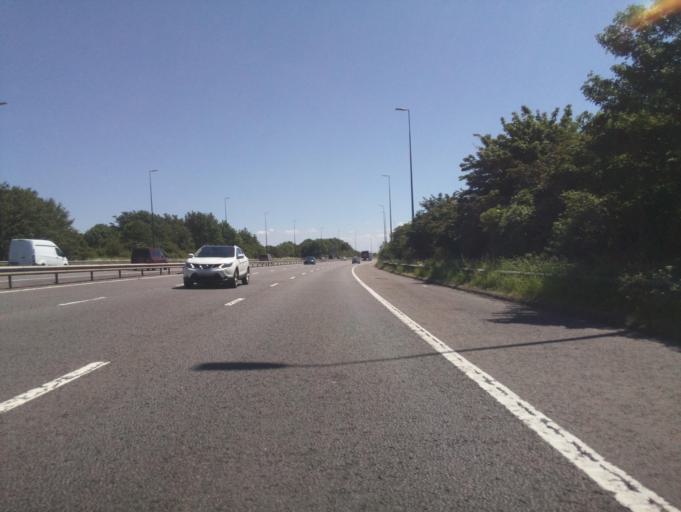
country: GB
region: Wales
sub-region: Monmouthshire
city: Rogiet
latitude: 51.5906
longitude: -2.8044
